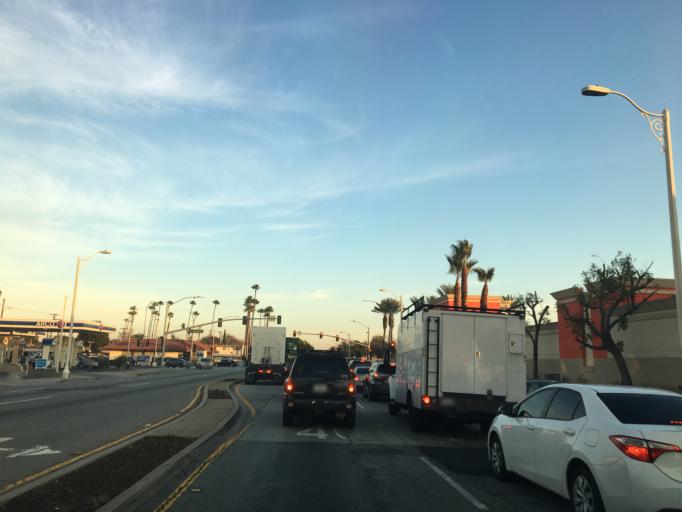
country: US
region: California
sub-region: Los Angeles County
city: Pico Rivera
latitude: 33.9881
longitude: -118.1061
